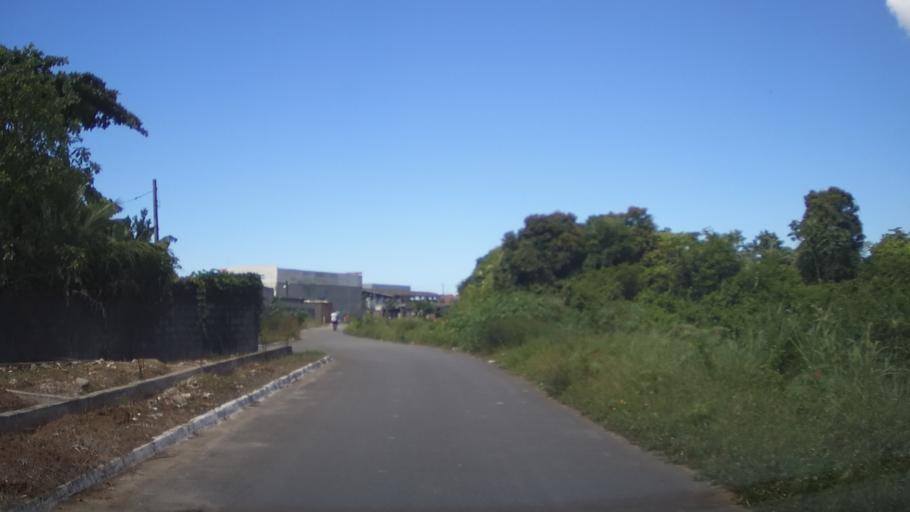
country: BR
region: Sao Paulo
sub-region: Praia Grande
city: Praia Grande
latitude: -24.0212
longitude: -46.5133
